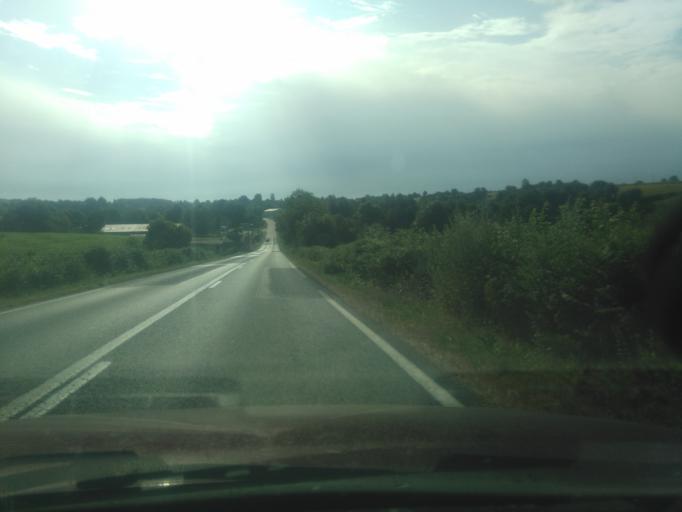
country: FR
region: Pays de la Loire
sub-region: Departement de la Vendee
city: La Tardiere
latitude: 46.6526
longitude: -0.6946
